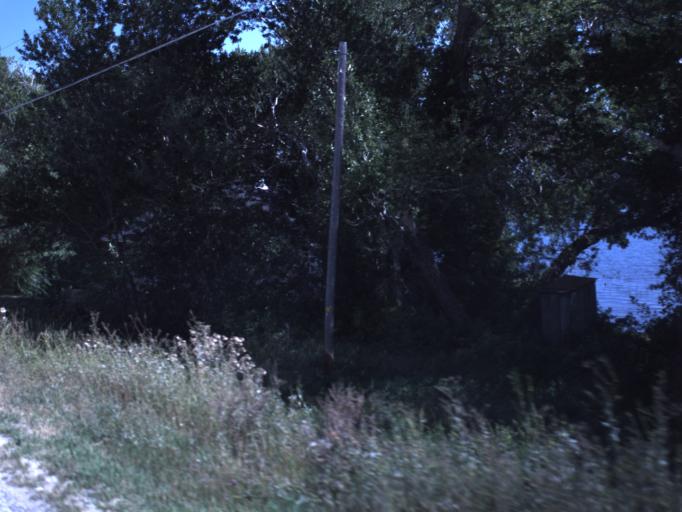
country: US
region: Idaho
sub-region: Bear Lake County
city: Paris
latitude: 41.9977
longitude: -111.4096
